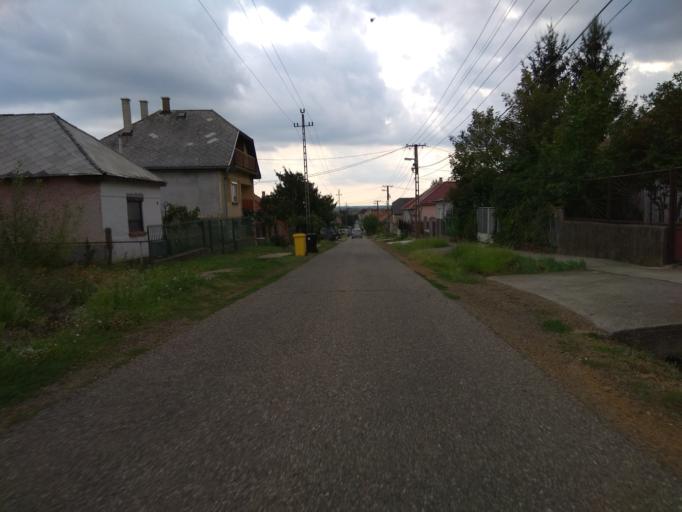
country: HU
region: Borsod-Abauj-Zemplen
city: Bekecs
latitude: 48.1527
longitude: 21.1626
